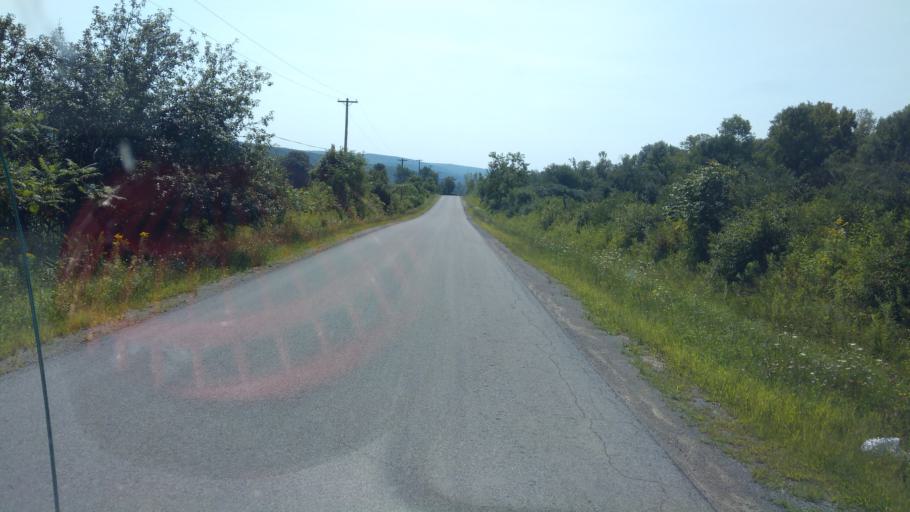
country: US
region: New York
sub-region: Allegany County
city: Belmont
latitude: 42.3360
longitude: -78.0397
